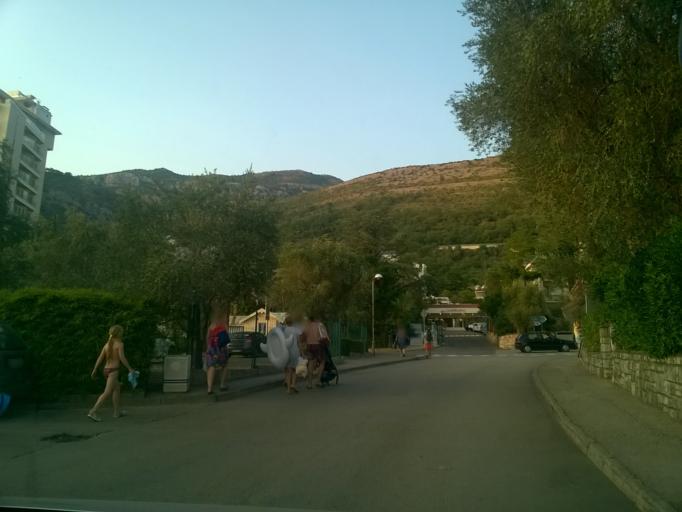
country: ME
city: Petrovac na Moru
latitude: 42.2063
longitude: 18.9434
